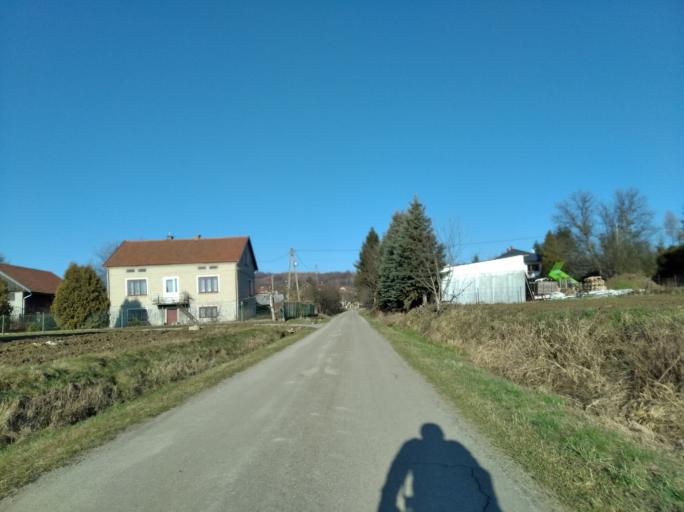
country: PL
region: Subcarpathian Voivodeship
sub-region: Powiat strzyzowski
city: Wisniowa
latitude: 49.8730
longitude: 21.6952
